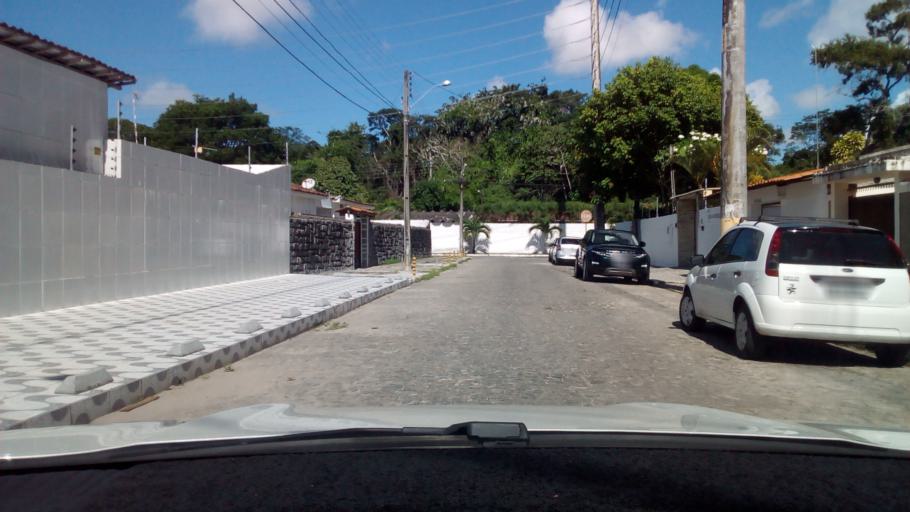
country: BR
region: Paraiba
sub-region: Joao Pessoa
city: Joao Pessoa
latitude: -7.1353
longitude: -34.8709
